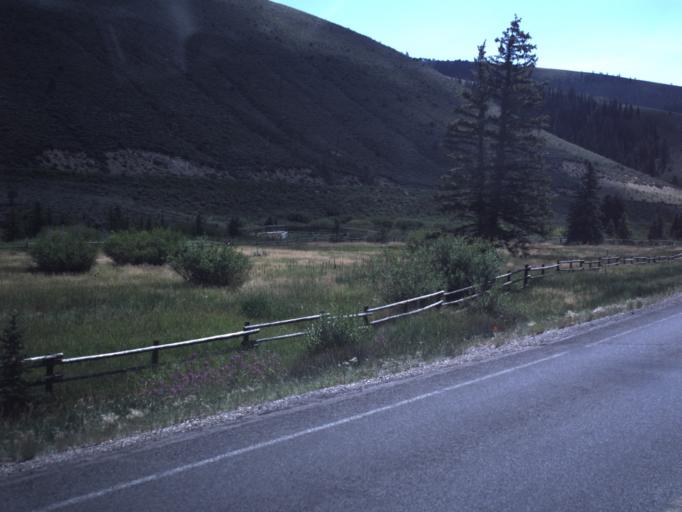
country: US
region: Utah
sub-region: Sanpete County
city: Fairview
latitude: 39.7037
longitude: -111.1615
